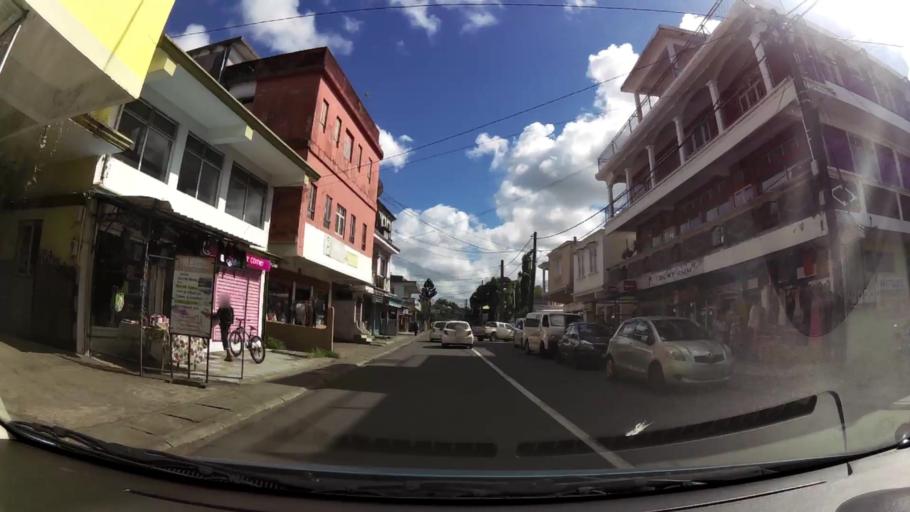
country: MU
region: Grand Port
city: Plaine Magnien
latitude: -20.4317
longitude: 57.6592
